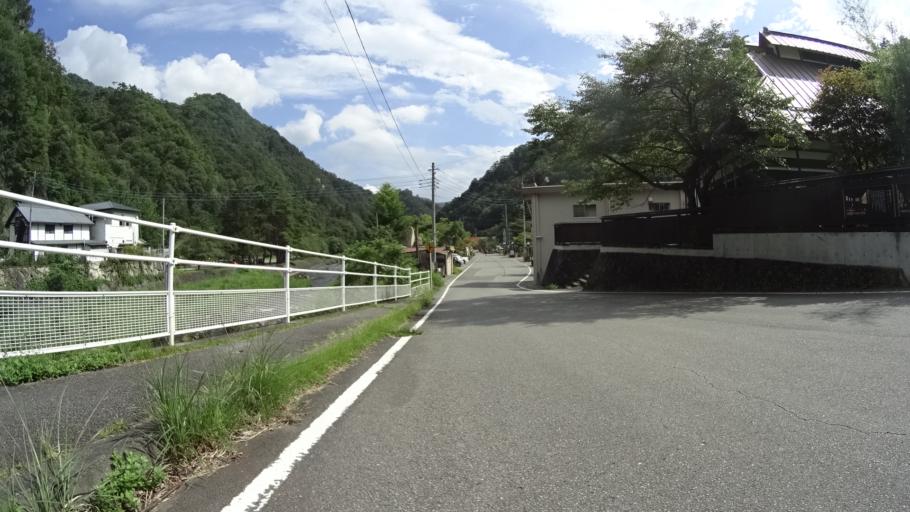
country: JP
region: Yamanashi
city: Kofu-shi
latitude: 35.7548
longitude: 138.5643
